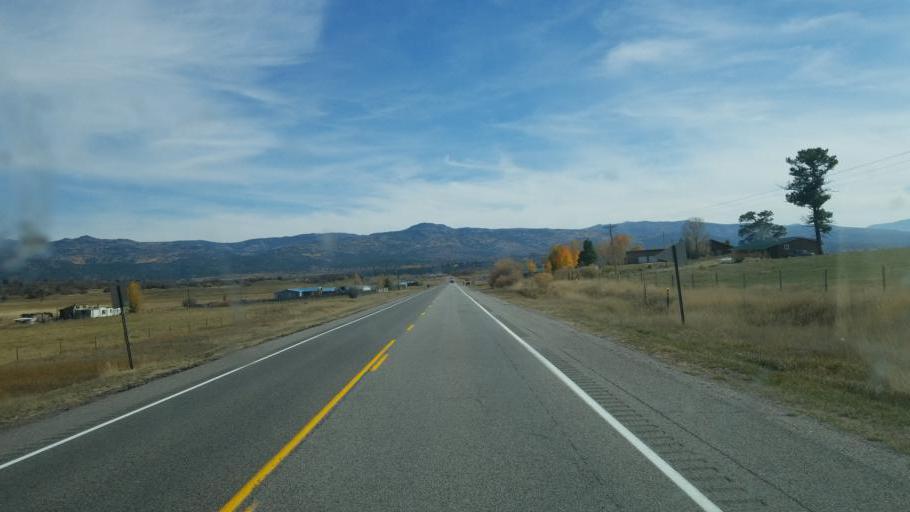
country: US
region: New Mexico
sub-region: Rio Arriba County
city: Chama
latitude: 36.8862
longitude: -106.6160
